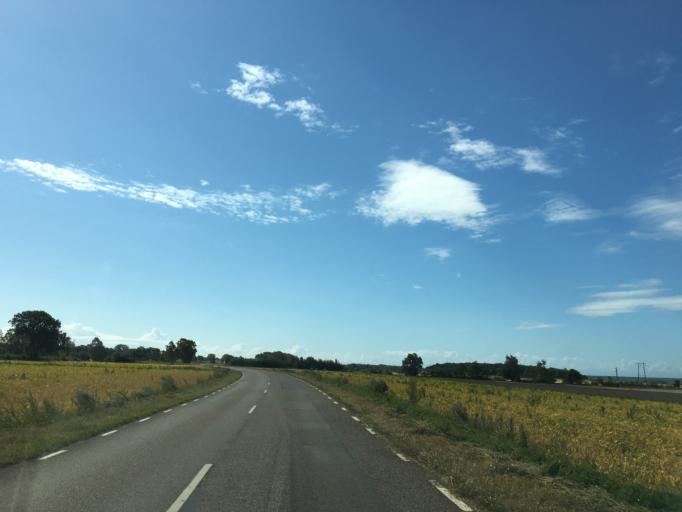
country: SE
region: Kalmar
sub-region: Morbylanga Kommun
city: Moerbylanga
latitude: 56.4140
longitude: 16.4136
